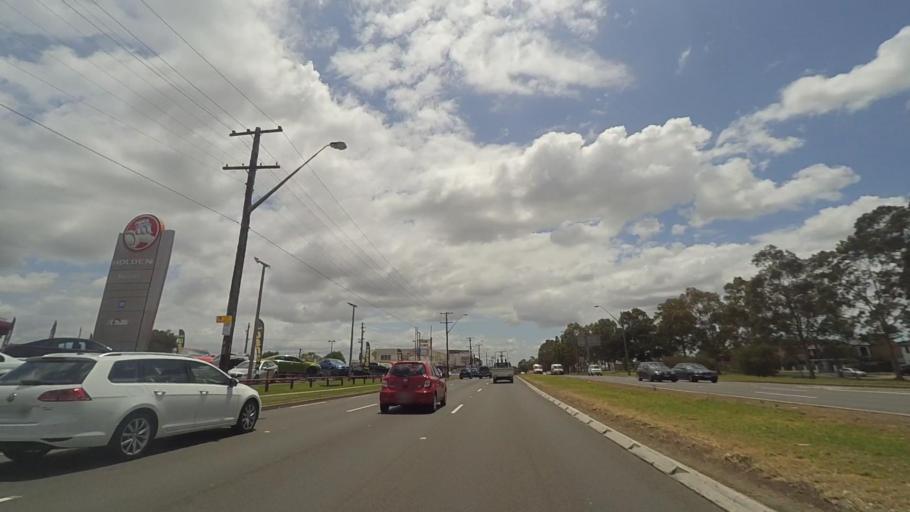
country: AU
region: New South Wales
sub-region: Campbelltown Municipality
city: Glenfield
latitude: -33.9372
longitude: 150.9140
